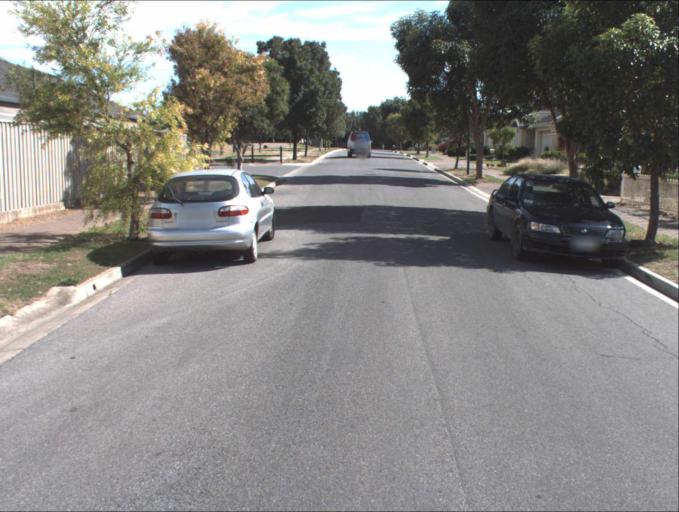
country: AU
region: South Australia
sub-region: Port Adelaide Enfield
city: Gilles Plains
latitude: -34.8634
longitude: 138.6545
